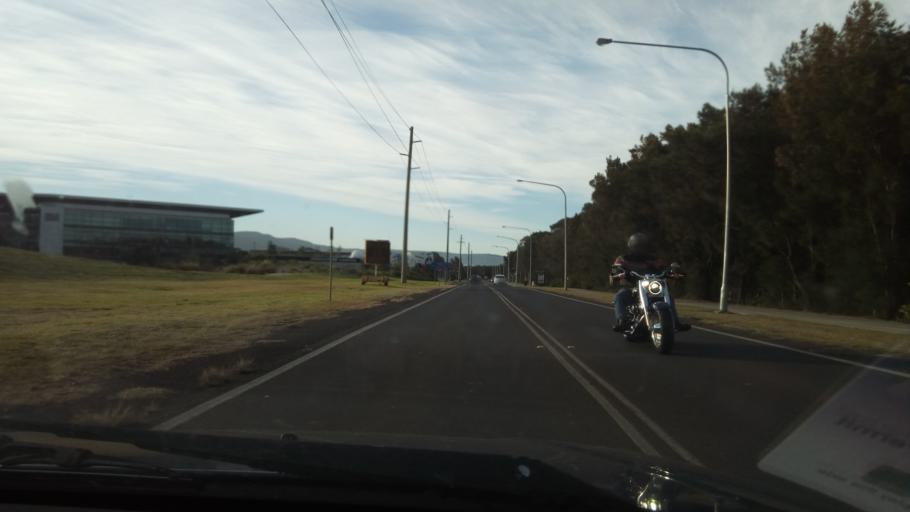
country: AU
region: New South Wales
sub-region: Wollongong
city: Fairy Meadow
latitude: -34.4043
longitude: 150.8999
